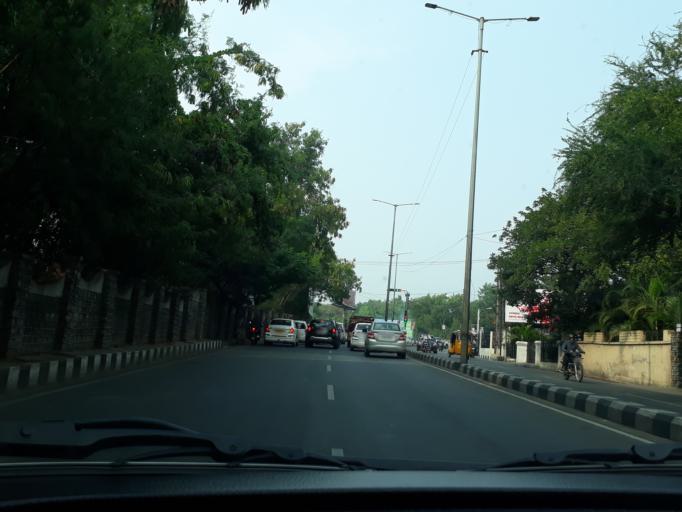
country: IN
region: Telangana
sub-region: Hyderabad
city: Malkajgiri
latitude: 17.4479
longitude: 78.4922
